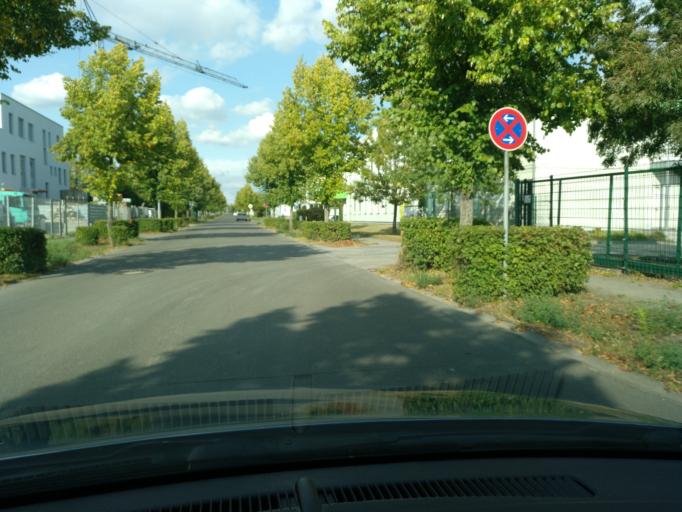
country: DE
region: Berlin
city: Mahlsdorf
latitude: 52.5066
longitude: 13.6323
